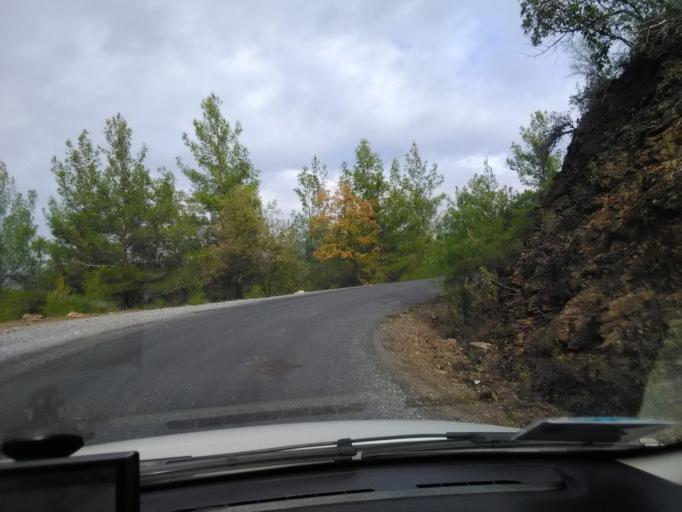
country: TR
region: Antalya
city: Gazipasa
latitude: 36.2435
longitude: 32.4186
